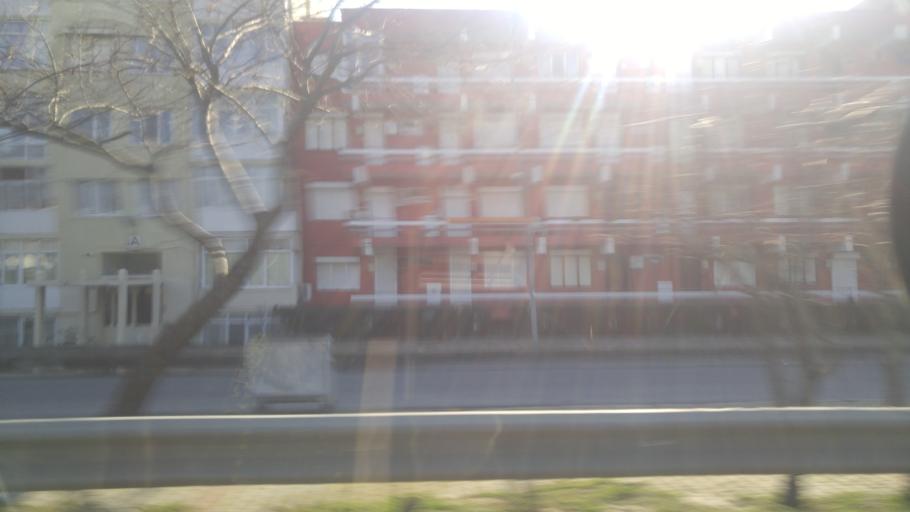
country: TR
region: Istanbul
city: Celaliye
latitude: 41.0461
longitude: 28.4058
